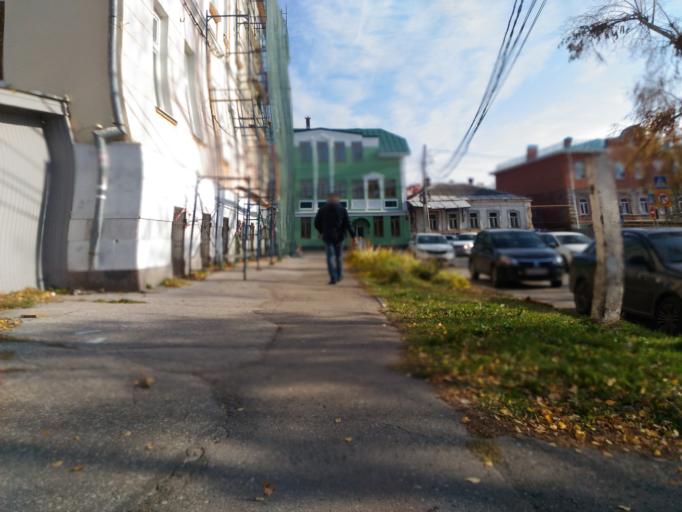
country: RU
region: Ulyanovsk
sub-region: Ulyanovskiy Rayon
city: Ulyanovsk
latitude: 54.3240
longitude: 48.3953
